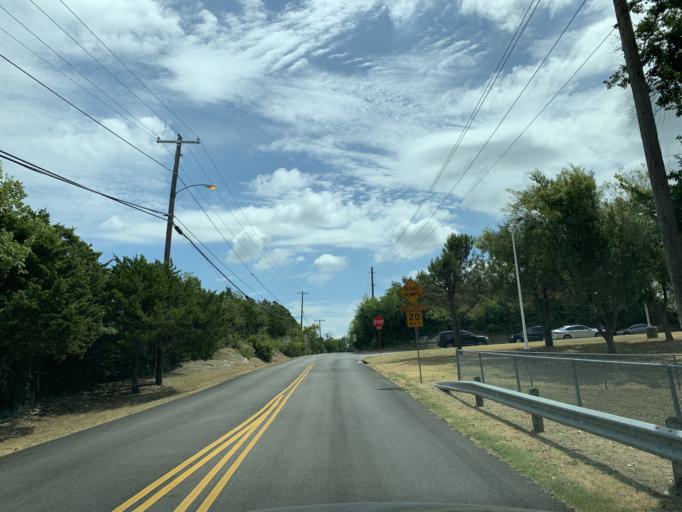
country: US
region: Texas
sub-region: Dallas County
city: Cockrell Hill
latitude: 32.7640
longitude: -96.8647
